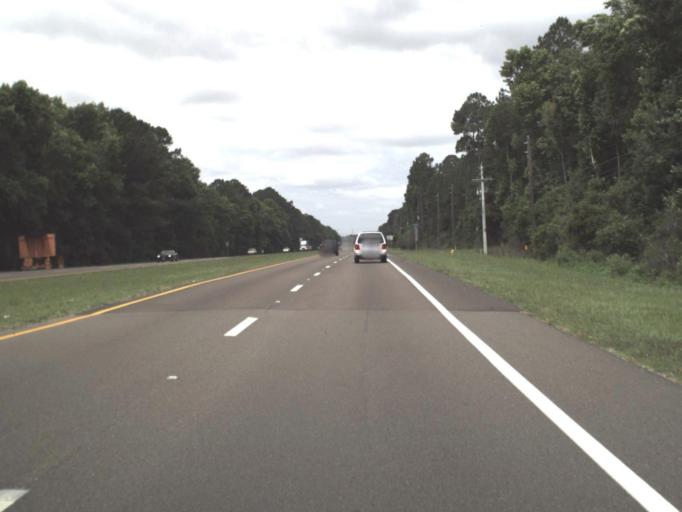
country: US
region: Florida
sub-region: Nassau County
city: Yulee
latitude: 30.6298
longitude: -81.6105
